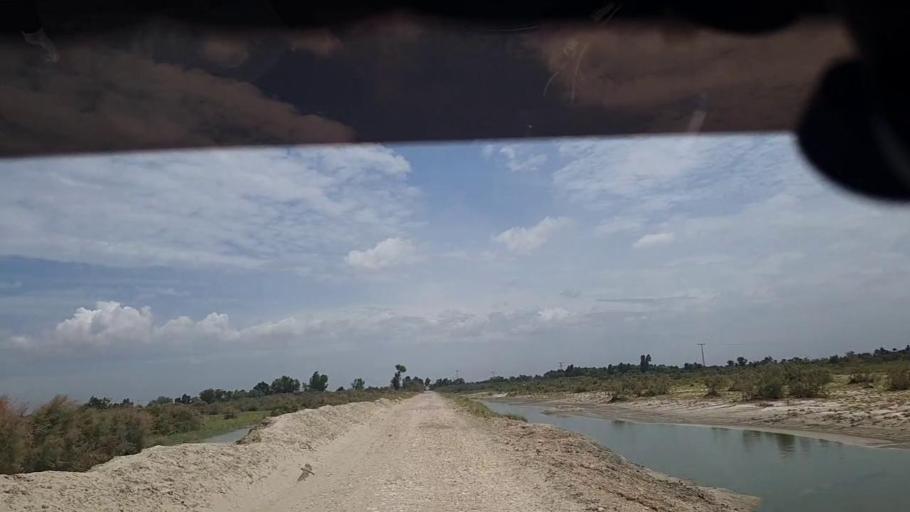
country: PK
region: Sindh
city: Rustam jo Goth
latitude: 28.0274
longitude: 68.9370
